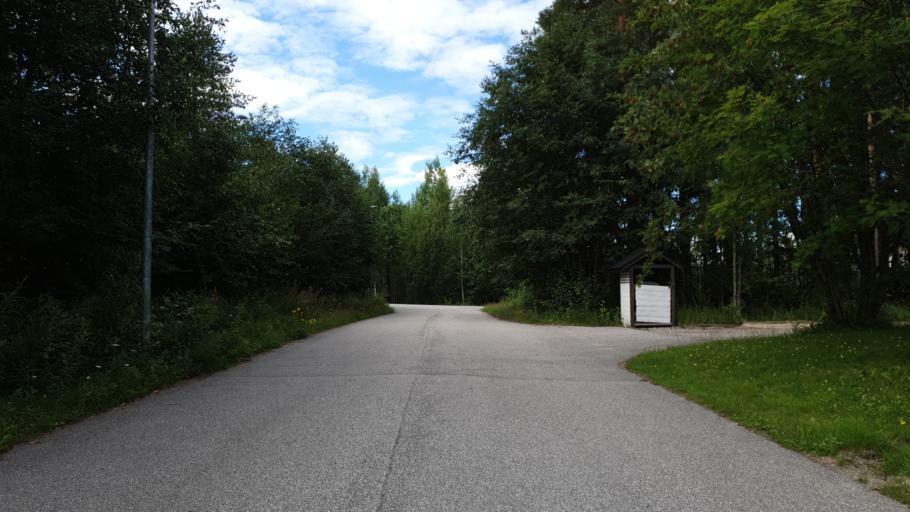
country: FI
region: Kainuu
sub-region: Kehys-Kainuu
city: Kuhmo
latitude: 64.1252
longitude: 29.5543
